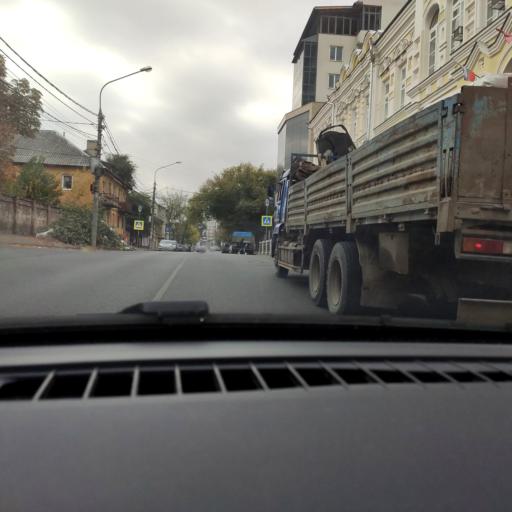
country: RU
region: Voronezj
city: Voronezh
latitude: 51.6771
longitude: 39.2179
